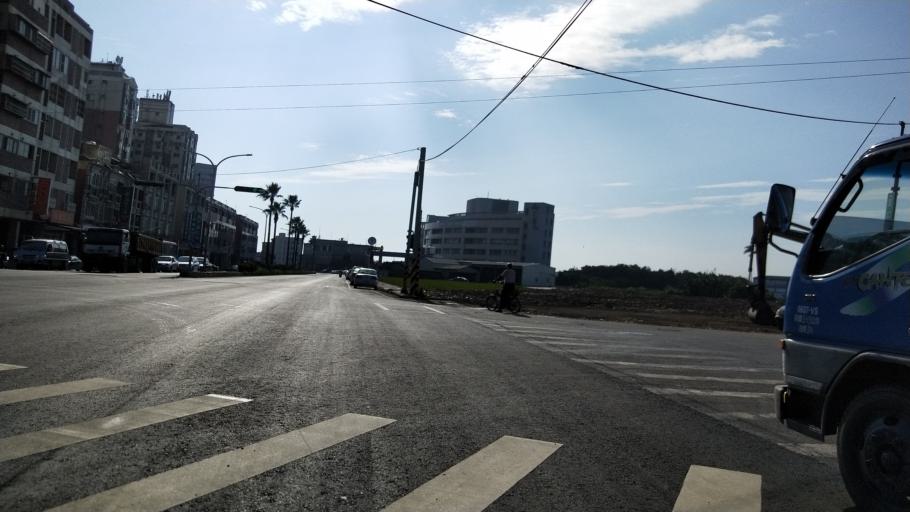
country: TW
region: Taiwan
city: Fengyuan
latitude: 24.3569
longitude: 120.6226
